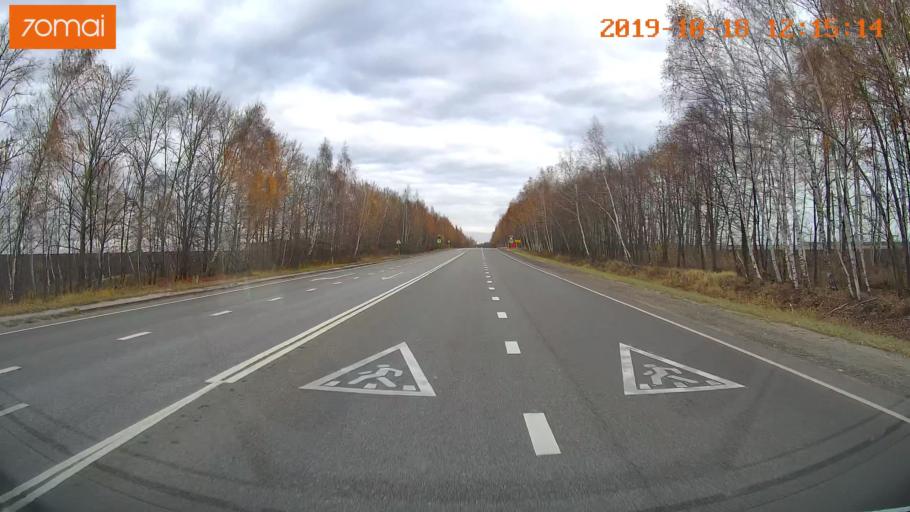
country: RU
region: Rjazan
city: Zakharovo
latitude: 54.4409
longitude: 39.3965
